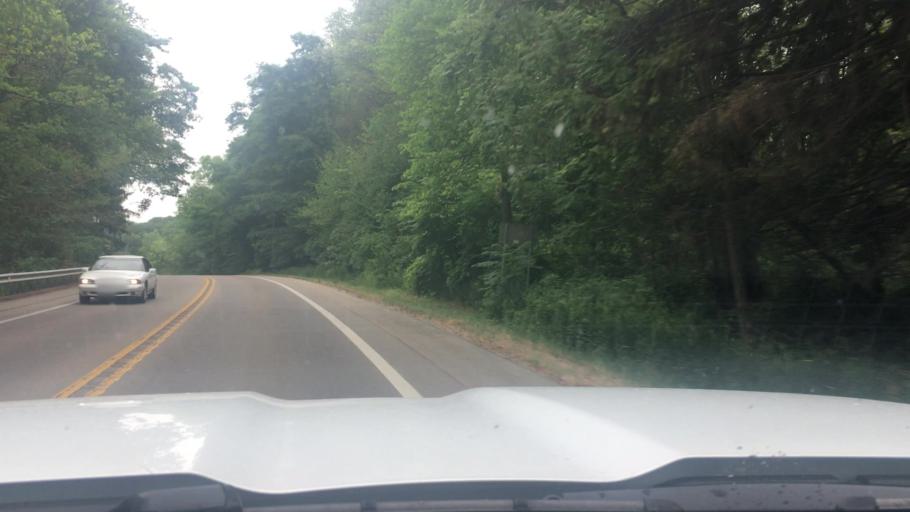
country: US
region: Michigan
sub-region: Ionia County
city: Ionia
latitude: 42.9764
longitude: -85.1212
